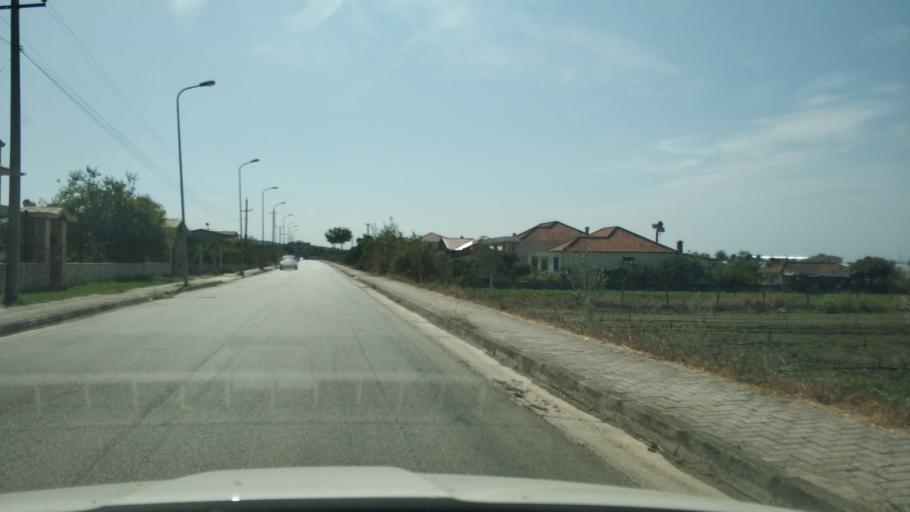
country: AL
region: Fier
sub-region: Rrethi i Lushnjes
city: Divjake
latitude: 40.9812
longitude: 19.5349
